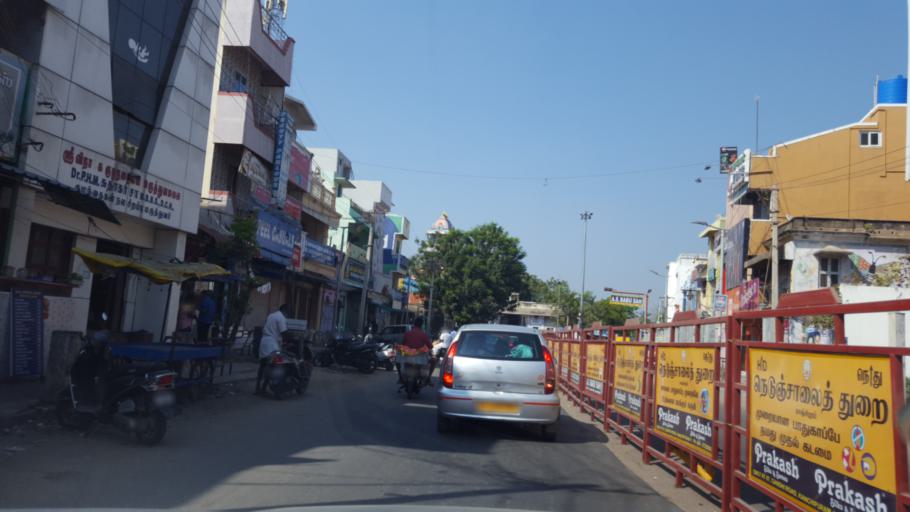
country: IN
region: Tamil Nadu
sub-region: Kancheepuram
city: Kanchipuram
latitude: 12.8427
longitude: 79.7011
